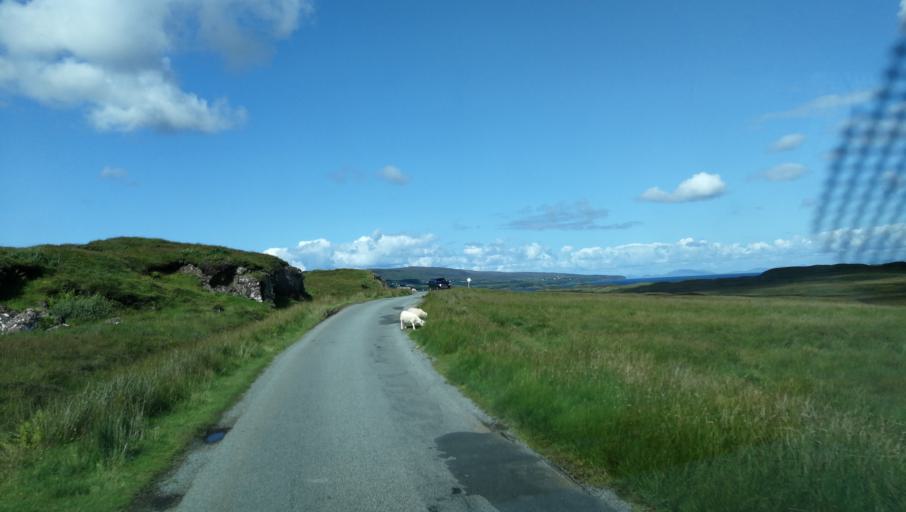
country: GB
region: Scotland
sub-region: Highland
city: Isle of Skye
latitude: 57.4270
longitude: -6.6038
